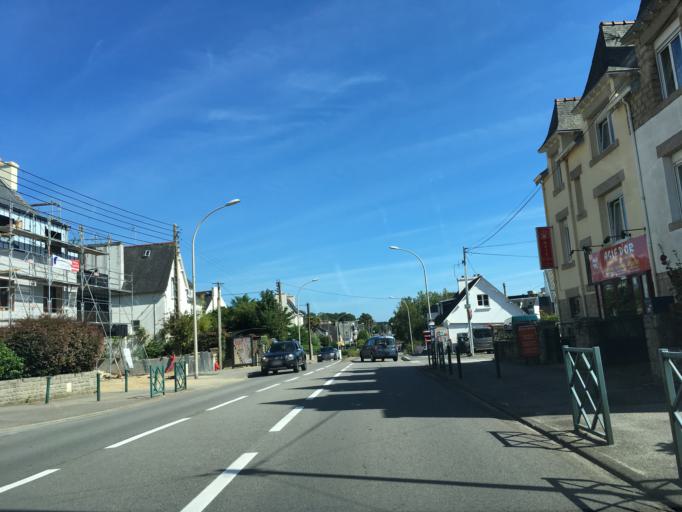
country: FR
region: Brittany
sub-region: Departement du Finistere
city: Quimper
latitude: 47.9855
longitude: -4.1065
